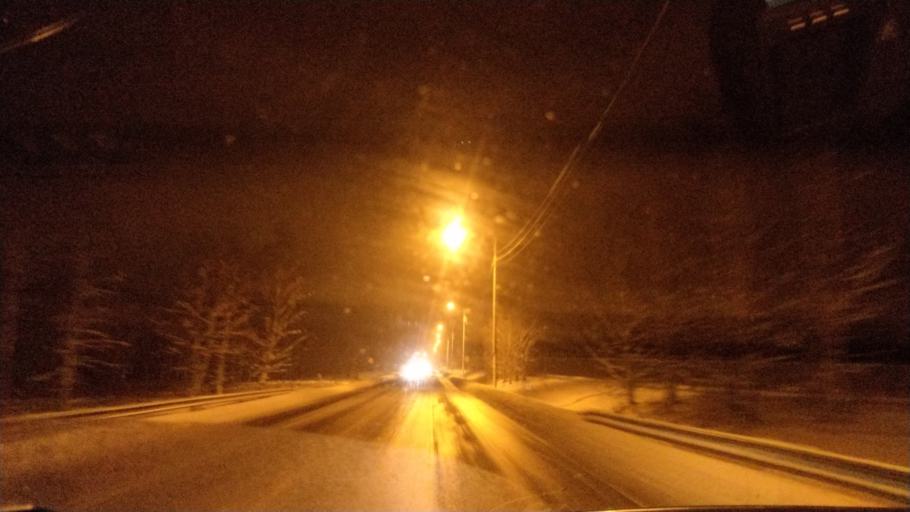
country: FI
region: Lapland
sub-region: Rovaniemi
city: Rovaniemi
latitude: 66.2807
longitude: 25.3359
